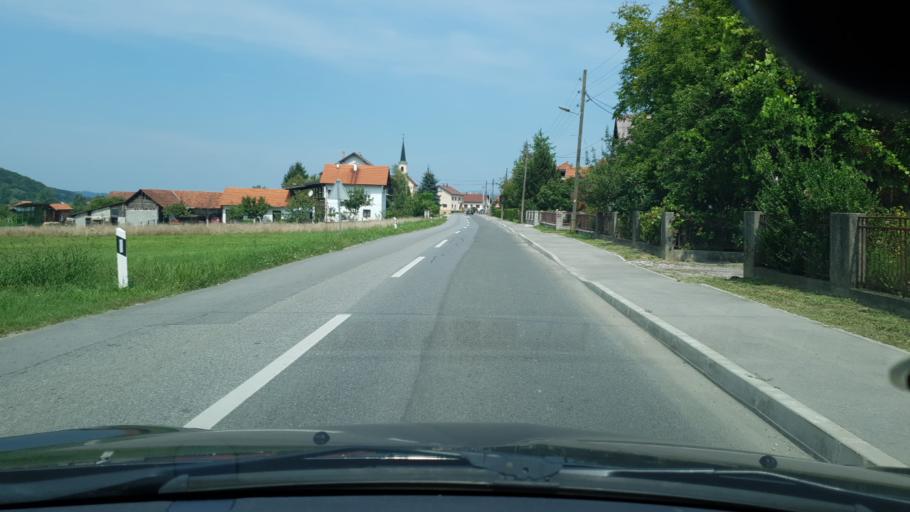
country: HR
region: Krapinsko-Zagorska
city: Marija Bistrica
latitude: 46.0249
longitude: 16.1024
